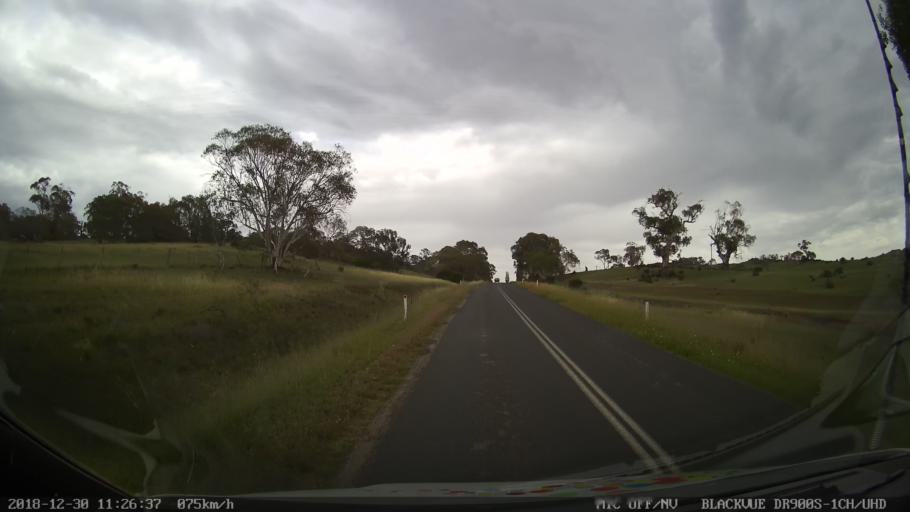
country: AU
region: New South Wales
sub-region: Snowy River
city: Jindabyne
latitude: -36.4669
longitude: 148.6321
